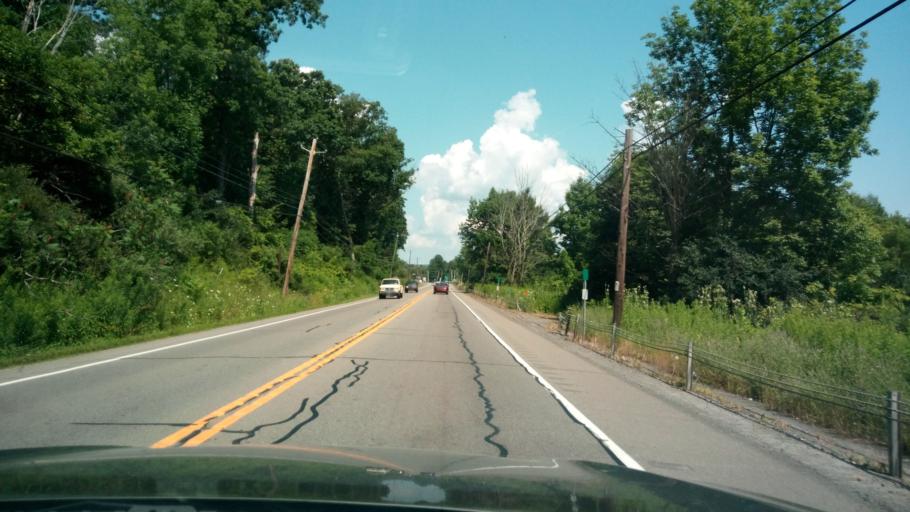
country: US
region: New York
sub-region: Chemung County
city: Horseheads
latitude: 42.1853
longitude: -76.8332
